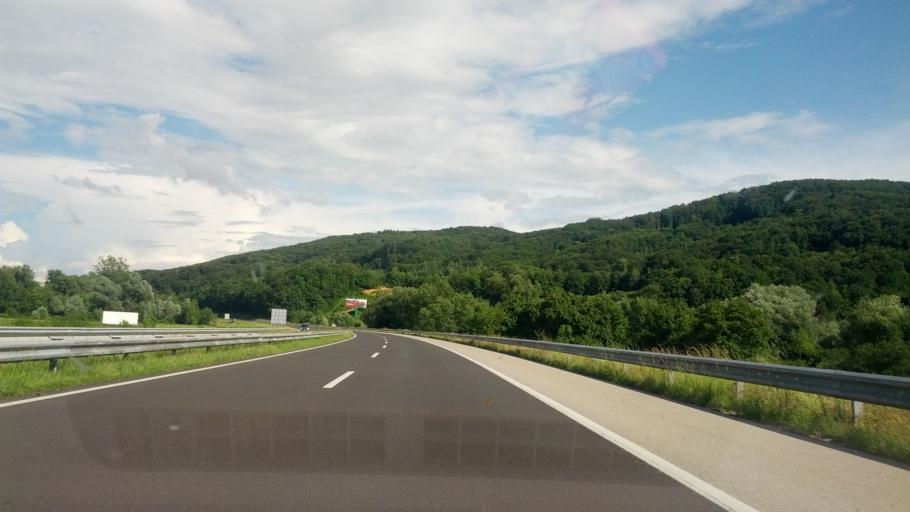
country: SI
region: Brezice
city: Brezice
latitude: 45.8822
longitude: 15.6221
